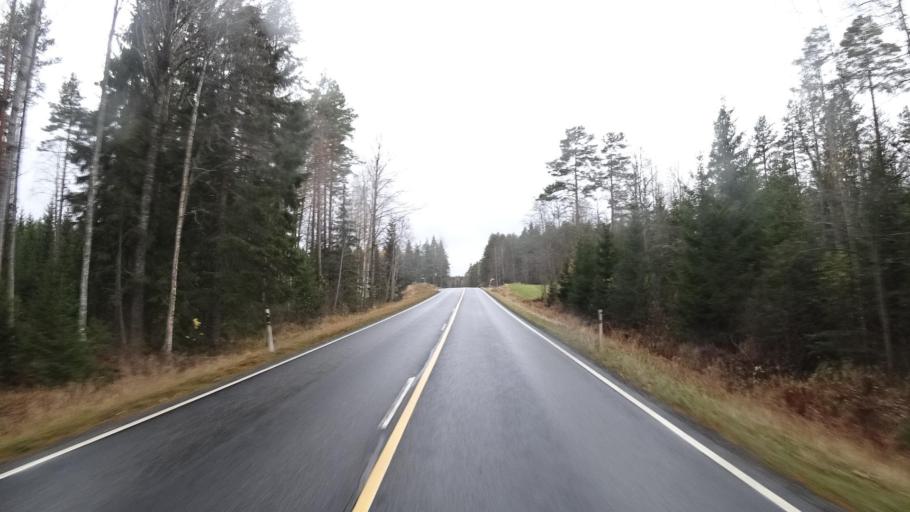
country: FI
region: Southern Savonia
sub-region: Mikkeli
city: Kangasniemi
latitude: 62.1616
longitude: 26.8338
